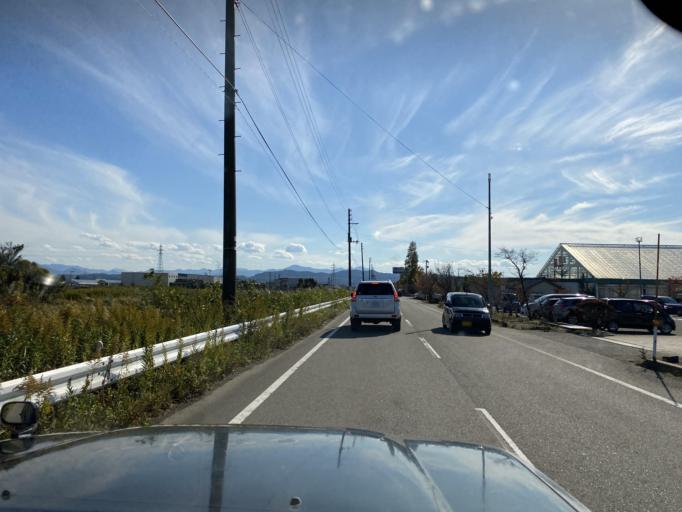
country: JP
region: Niigata
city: Niitsu-honcho
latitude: 37.7943
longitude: 139.0788
